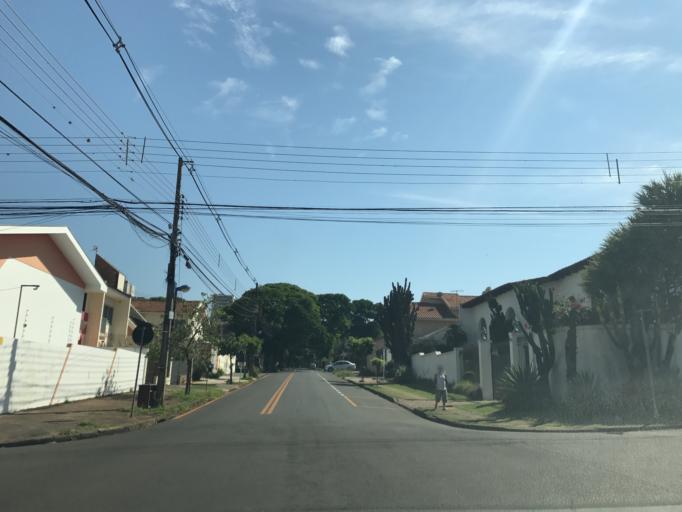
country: BR
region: Parana
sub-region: Maringa
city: Maringa
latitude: -23.4428
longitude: -51.9357
